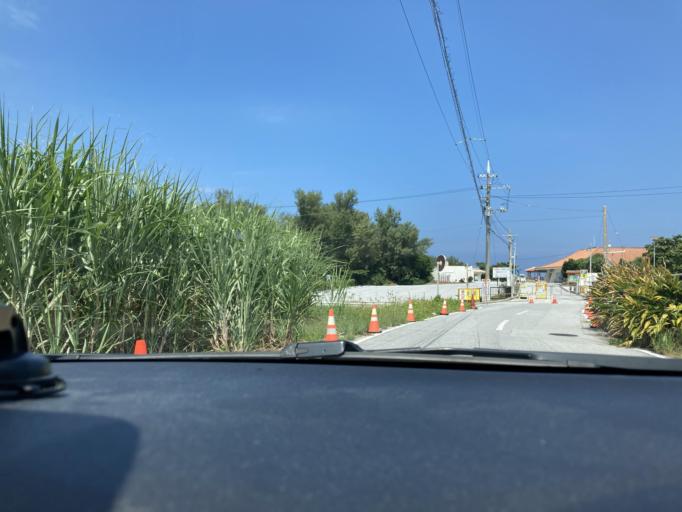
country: JP
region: Okinawa
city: Ishikawa
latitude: 26.4423
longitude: 127.7715
